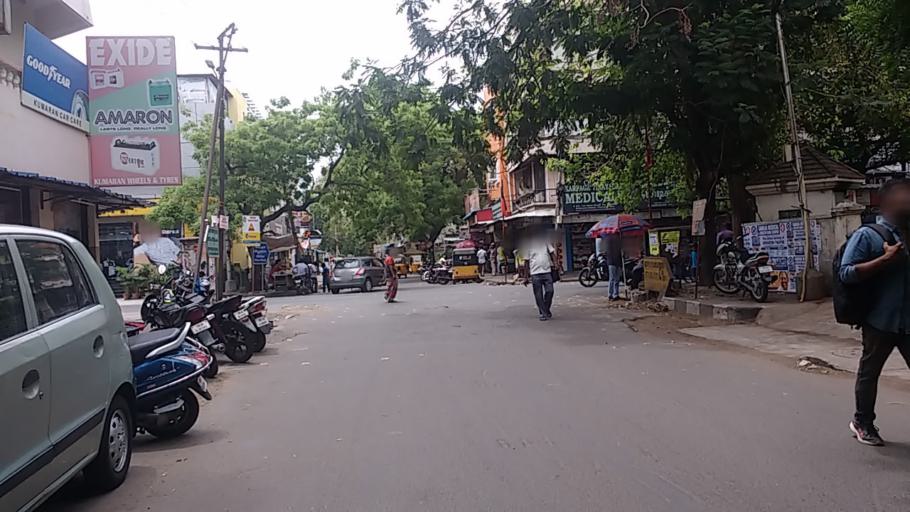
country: IN
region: Tamil Nadu
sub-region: Chennai
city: Chetput
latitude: 13.0524
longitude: 80.2273
